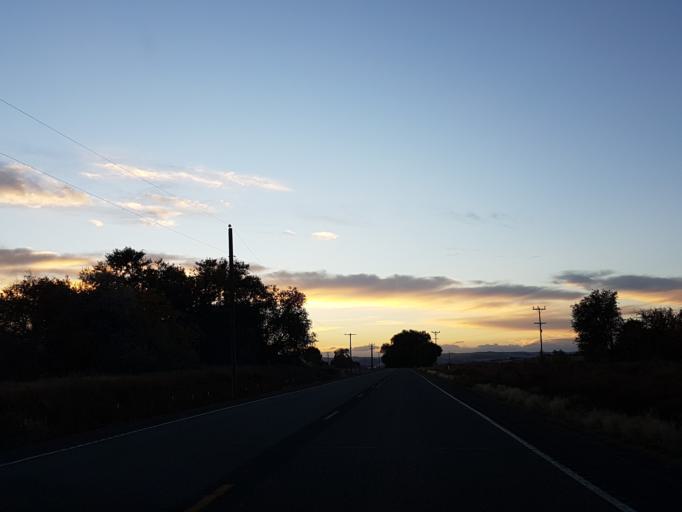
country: US
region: Oregon
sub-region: Malheur County
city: Vale
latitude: 43.9382
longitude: -117.3288
